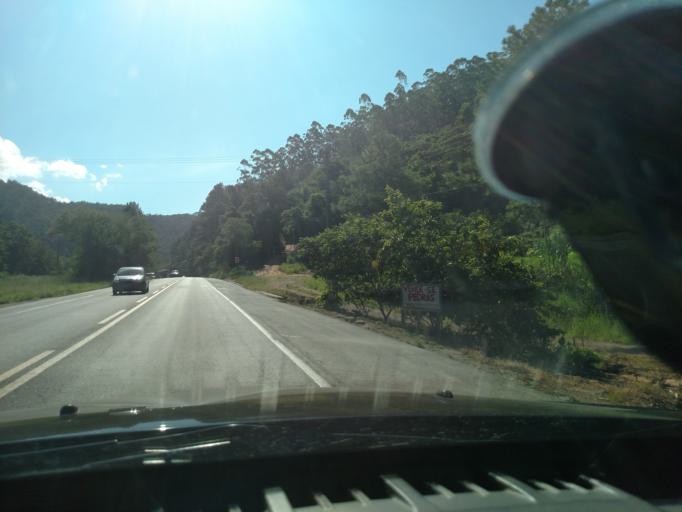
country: BR
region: Santa Catarina
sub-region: Ibirama
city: Ibirama
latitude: -27.0777
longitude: -49.4931
